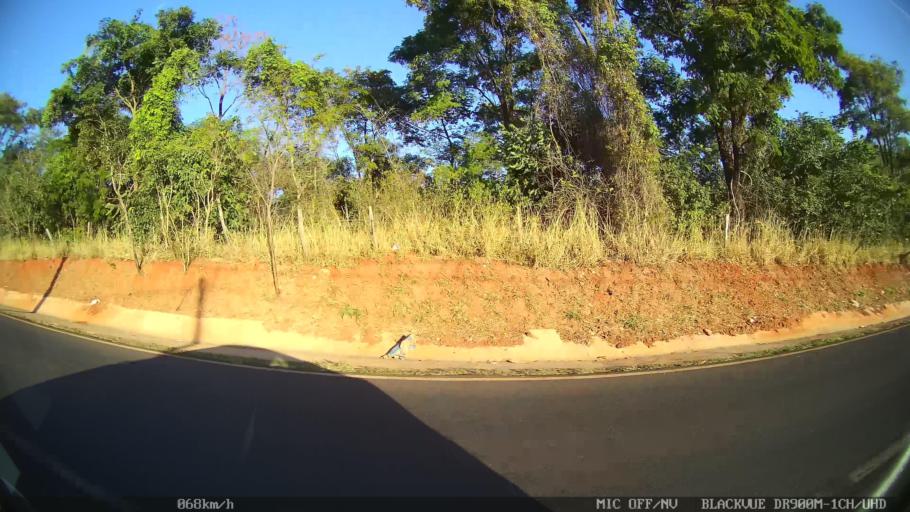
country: BR
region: Sao Paulo
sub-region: Sao Jose Do Rio Preto
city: Sao Jose do Rio Preto
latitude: -20.7684
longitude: -49.3573
